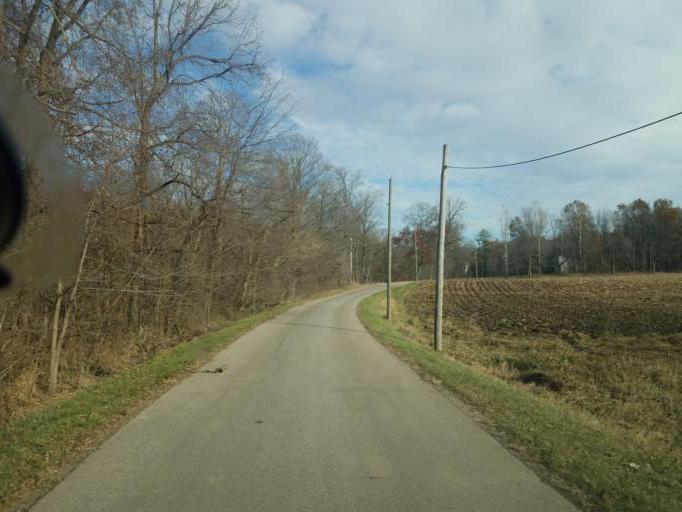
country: US
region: Ohio
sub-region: Crawford County
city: Bucyrus
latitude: 40.7105
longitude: -82.9361
